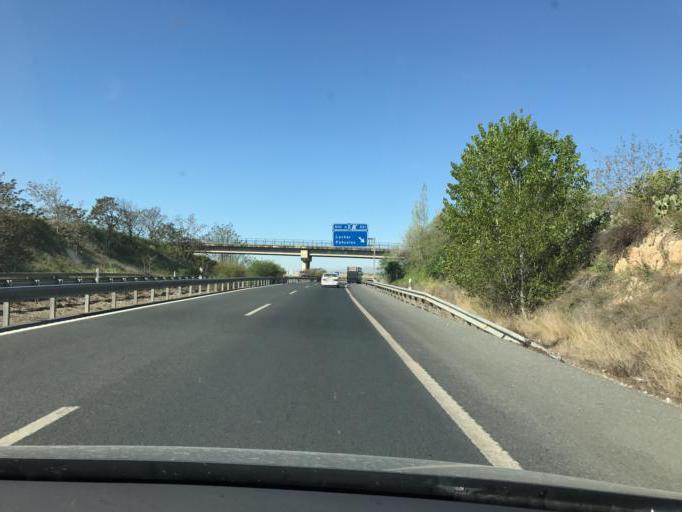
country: ES
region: Andalusia
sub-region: Provincia de Granada
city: Lachar
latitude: 37.1901
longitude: -3.8274
